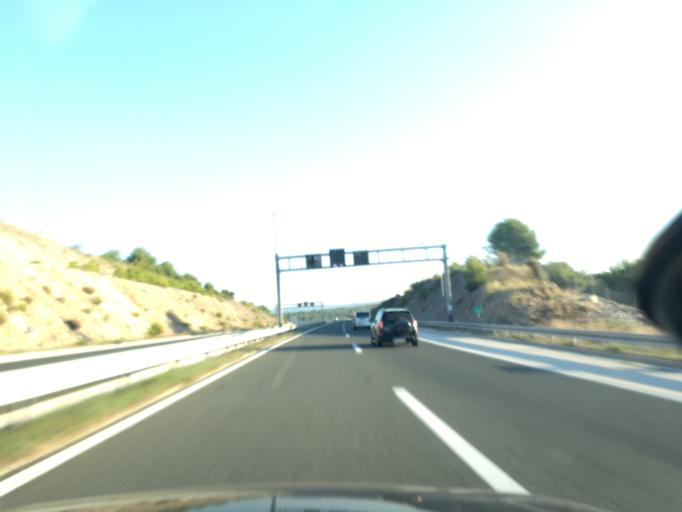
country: HR
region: Sibensko-Kniniska
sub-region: Grad Sibenik
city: Sibenik
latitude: 43.7868
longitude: 15.9183
